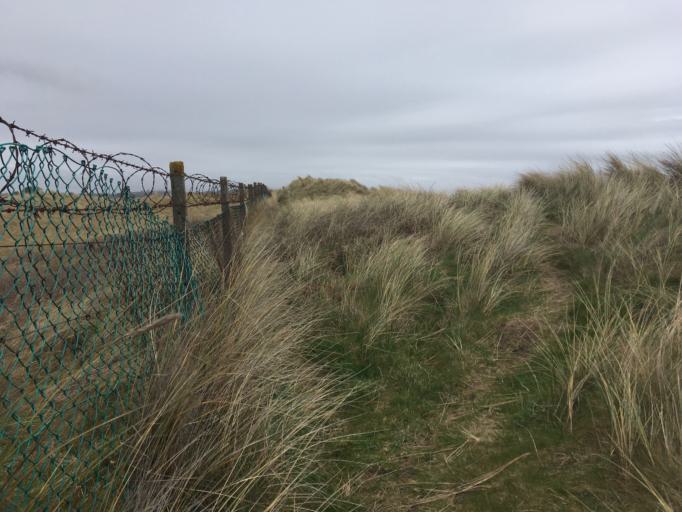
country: IE
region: Leinster
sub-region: Fingal County
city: Baldoyle
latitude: 53.4152
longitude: -6.1192
